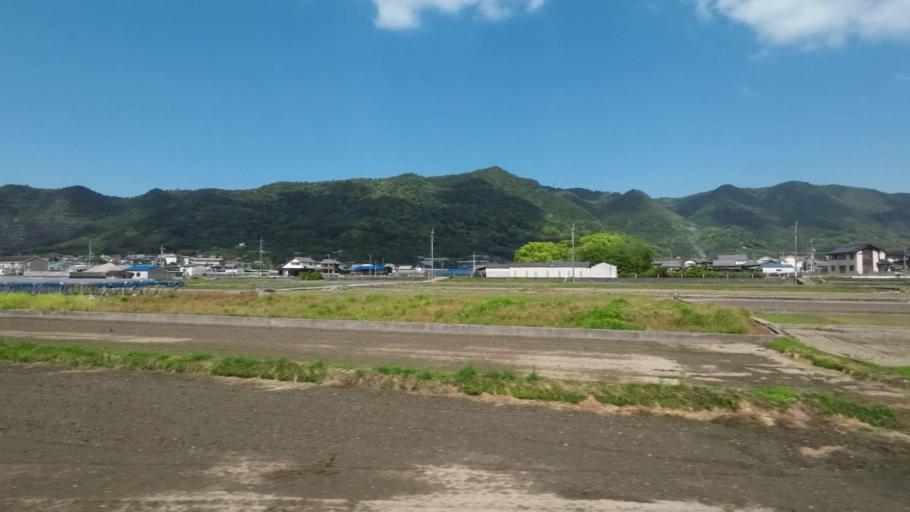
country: JP
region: Kagawa
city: Kan'onjicho
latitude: 34.1561
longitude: 133.6882
